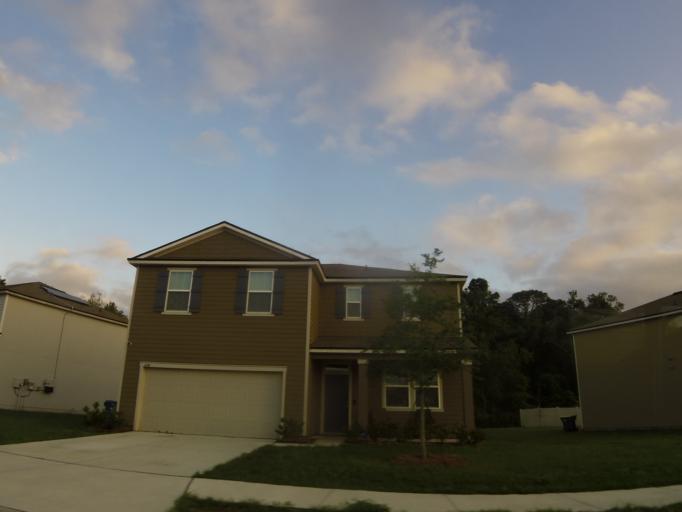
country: US
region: Florida
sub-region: Duval County
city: Jacksonville
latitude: 30.4710
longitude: -81.6228
